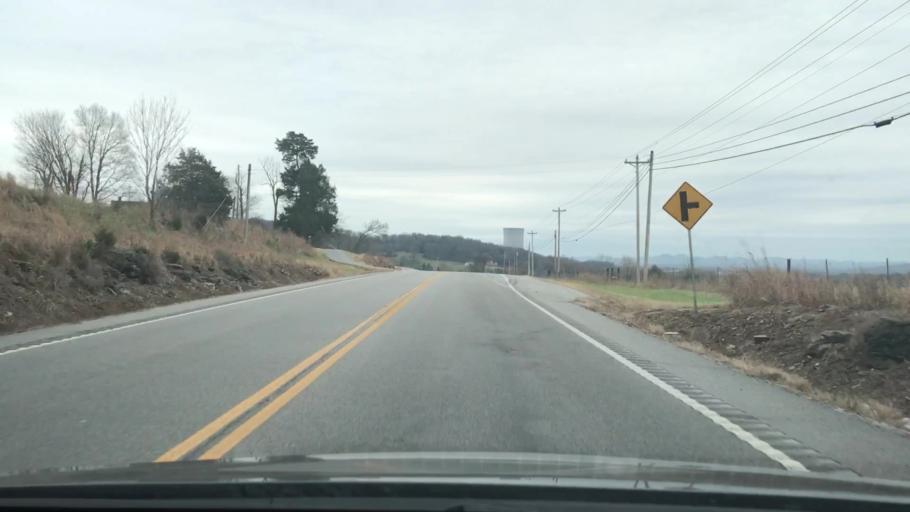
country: US
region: Tennessee
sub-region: Trousdale County
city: Hartsville
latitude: 36.3753
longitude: -86.1110
